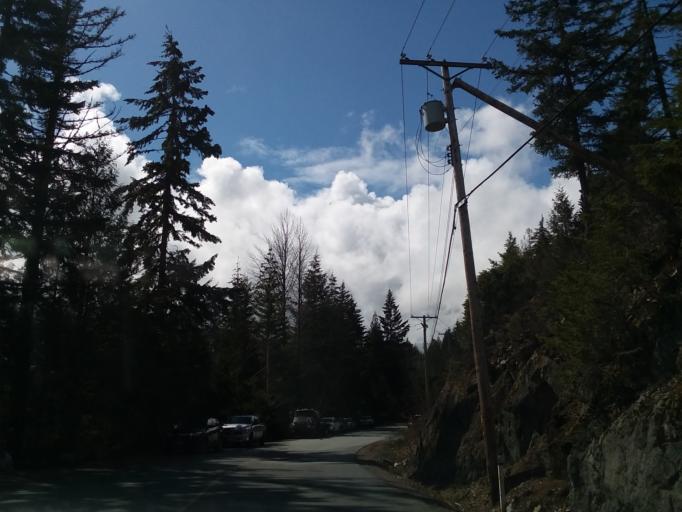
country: CA
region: British Columbia
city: Whistler
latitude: 50.1115
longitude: -122.9866
